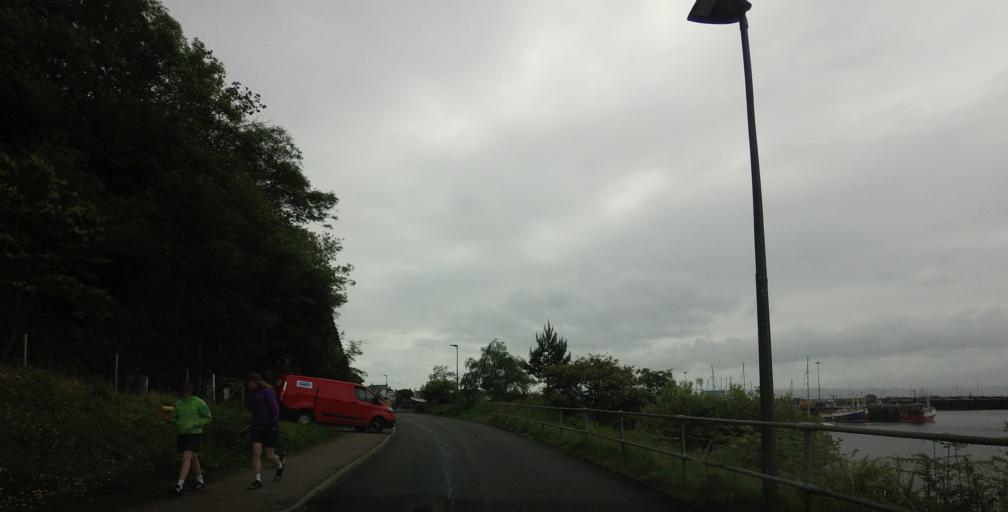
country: GB
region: Scotland
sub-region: Highland
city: Portree
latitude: 57.0043
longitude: -5.8247
